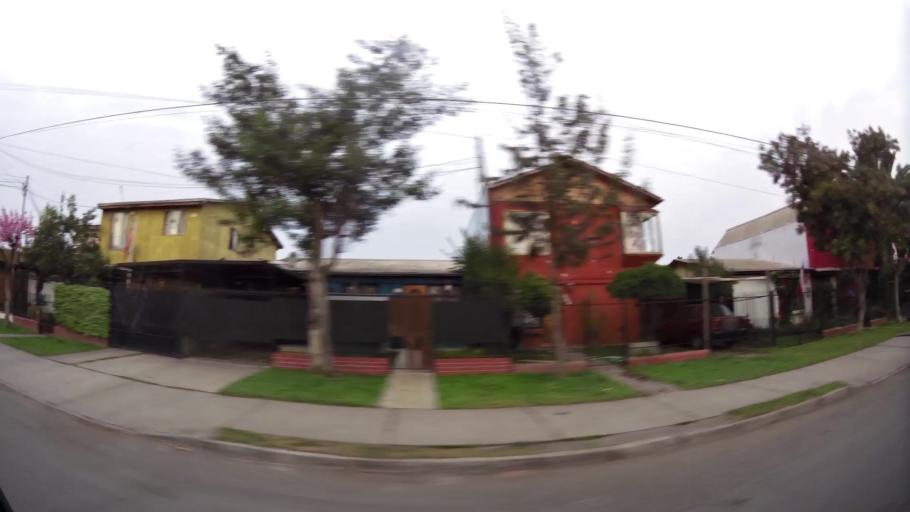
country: CL
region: Santiago Metropolitan
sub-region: Provincia de Santiago
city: Lo Prado
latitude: -33.5240
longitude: -70.7868
